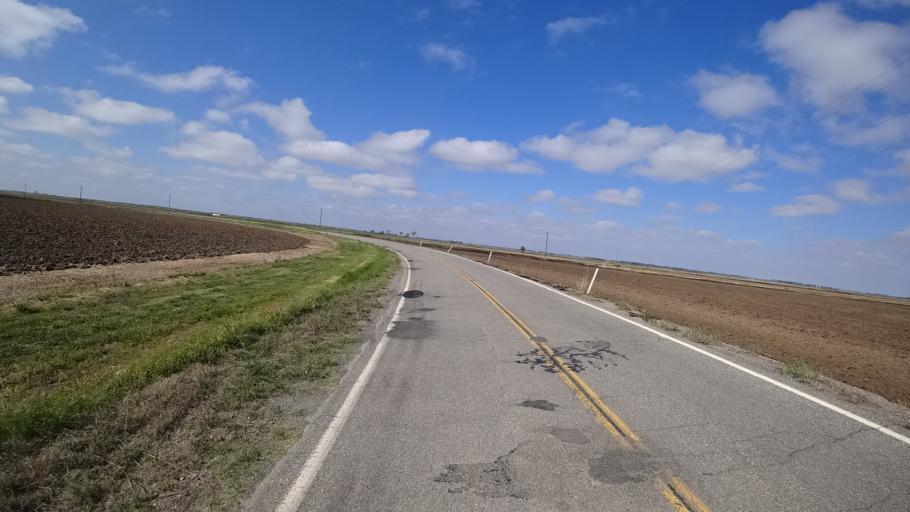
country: US
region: California
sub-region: Colusa County
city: Colusa
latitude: 39.3619
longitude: -121.9488
